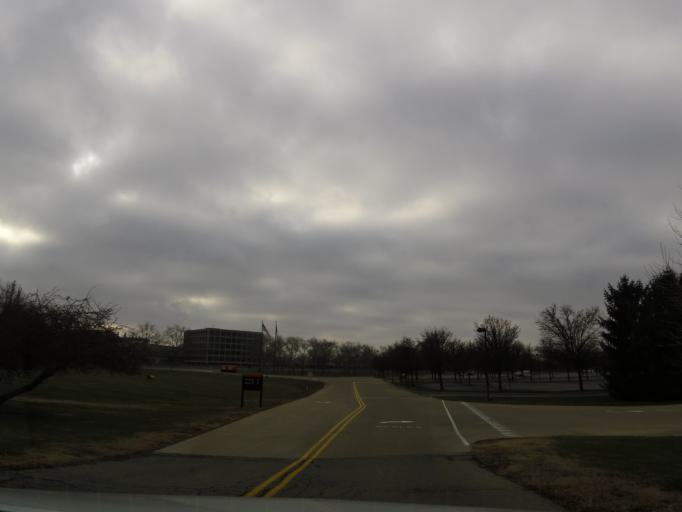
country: US
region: Indiana
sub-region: Bartholomew County
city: Columbus
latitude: 39.2046
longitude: -85.9057
